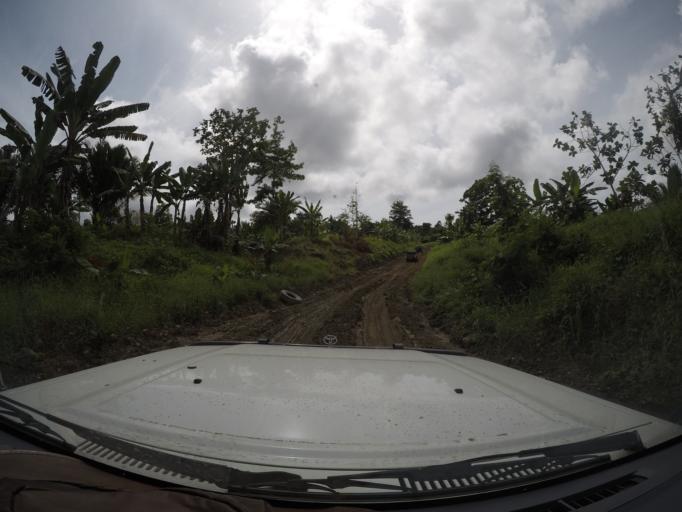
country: PG
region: Gulf
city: Kerema
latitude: -7.9950
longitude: 145.8297
